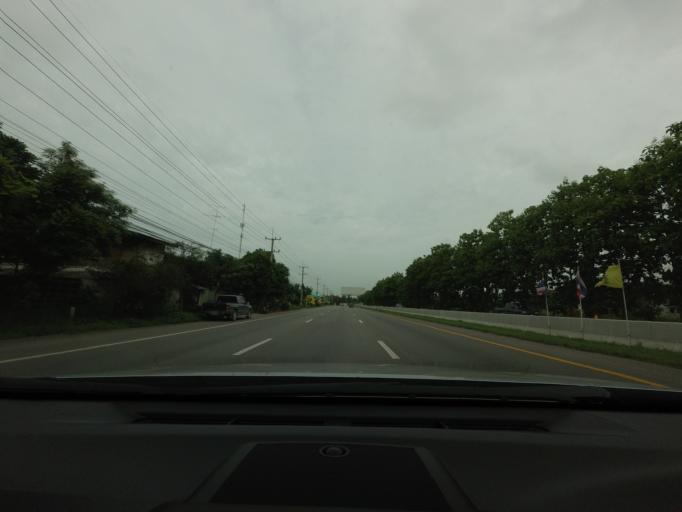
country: TH
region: Phetchaburi
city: Khao Yoi
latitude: 13.1672
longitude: 99.8415
